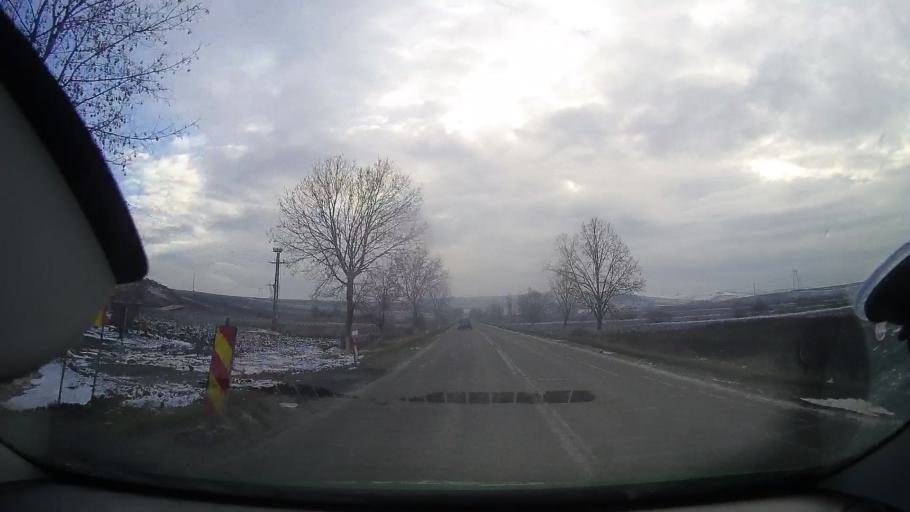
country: RO
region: Mures
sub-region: Comuna Iernut
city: Iernut
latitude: 46.4270
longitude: 24.2601
